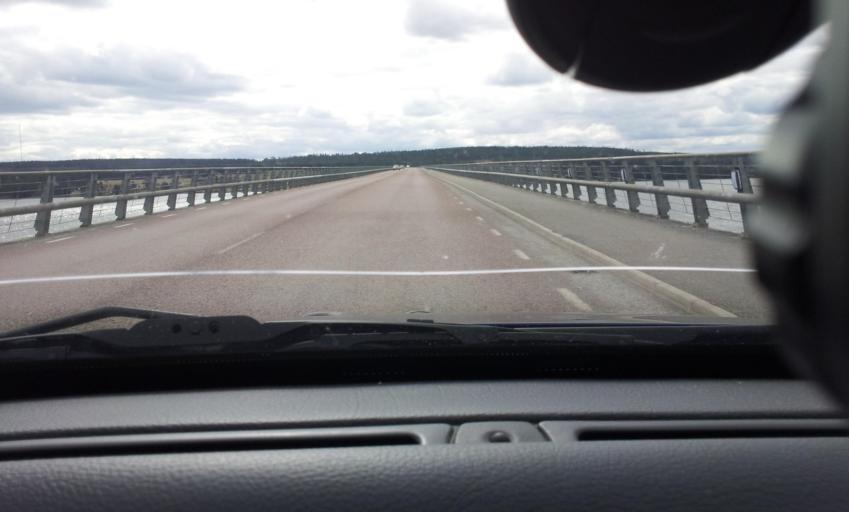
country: SE
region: Jaemtland
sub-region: OEstersunds Kommun
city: Ostersund
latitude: 63.1649
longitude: 14.6076
